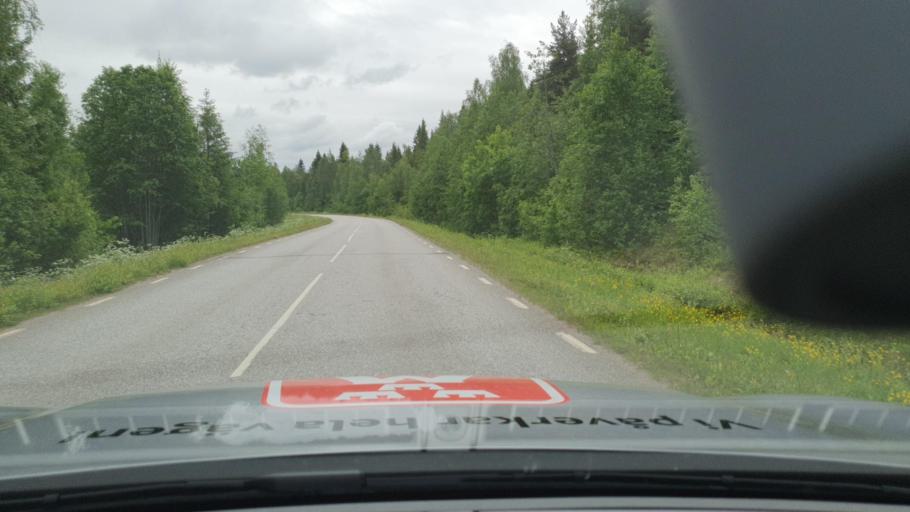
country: SE
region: Norrbotten
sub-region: Lulea Kommun
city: Ranea
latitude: 65.8836
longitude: 22.2017
